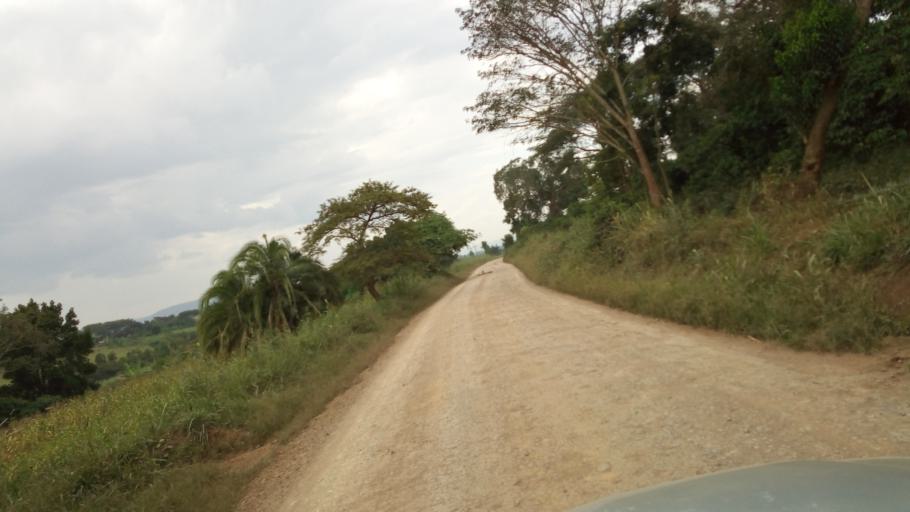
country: UG
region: Central Region
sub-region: Kiboga District
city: Kiboga
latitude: 0.7169
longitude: 31.7452
